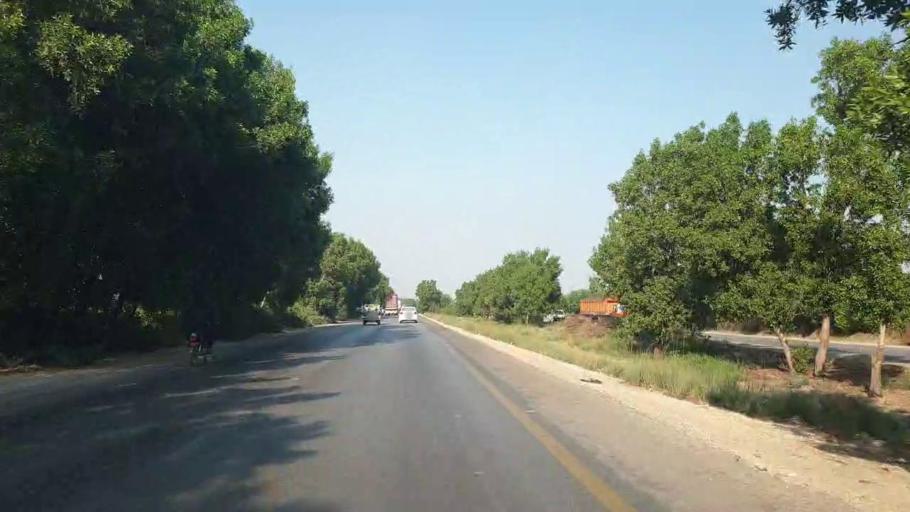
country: PK
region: Sindh
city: Matiari
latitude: 25.5051
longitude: 68.4264
